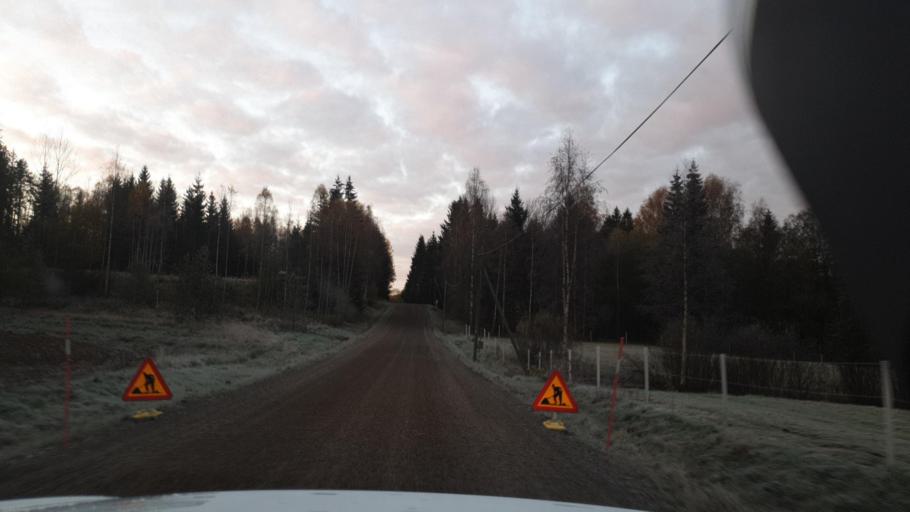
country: SE
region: Vaermland
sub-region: Eda Kommun
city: Amotfors
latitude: 59.7758
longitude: 12.3418
